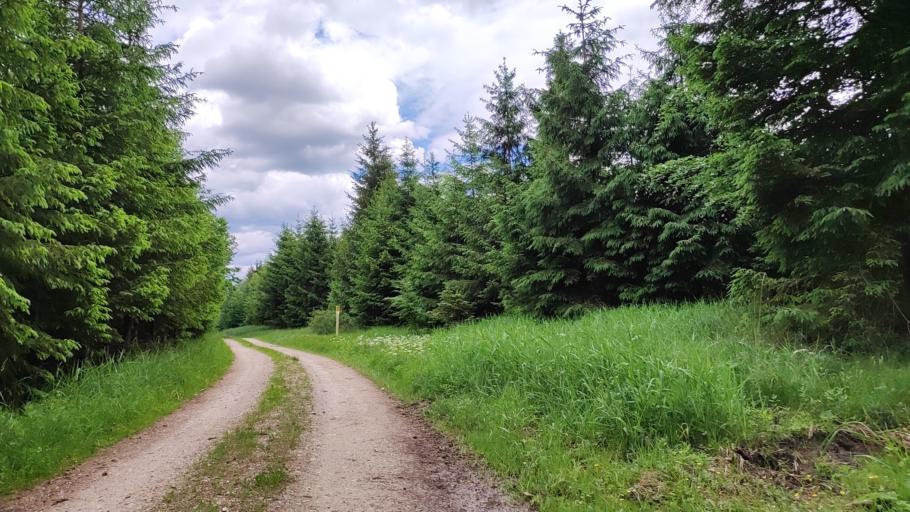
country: DE
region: Bavaria
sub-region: Swabia
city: Zusmarshausen
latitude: 48.3853
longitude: 10.5505
